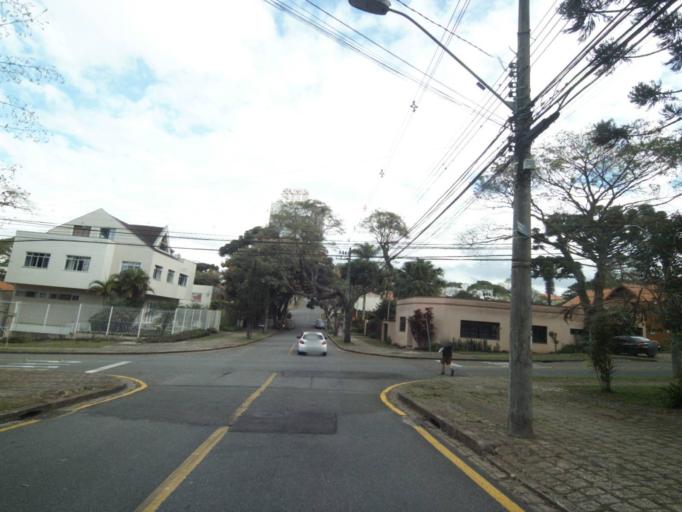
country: BR
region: Parana
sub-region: Curitiba
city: Curitiba
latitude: -25.4209
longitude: -49.2800
